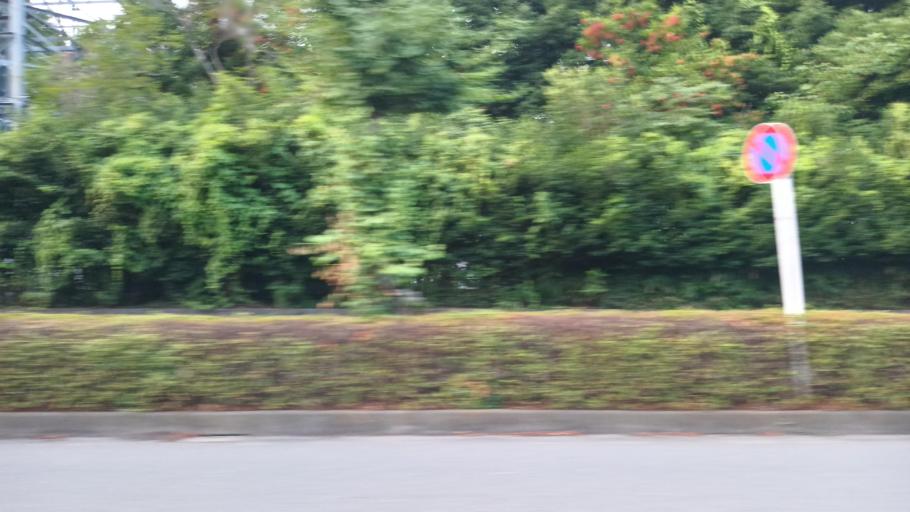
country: JP
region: Tokyo
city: Fussa
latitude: 35.7801
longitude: 139.3055
